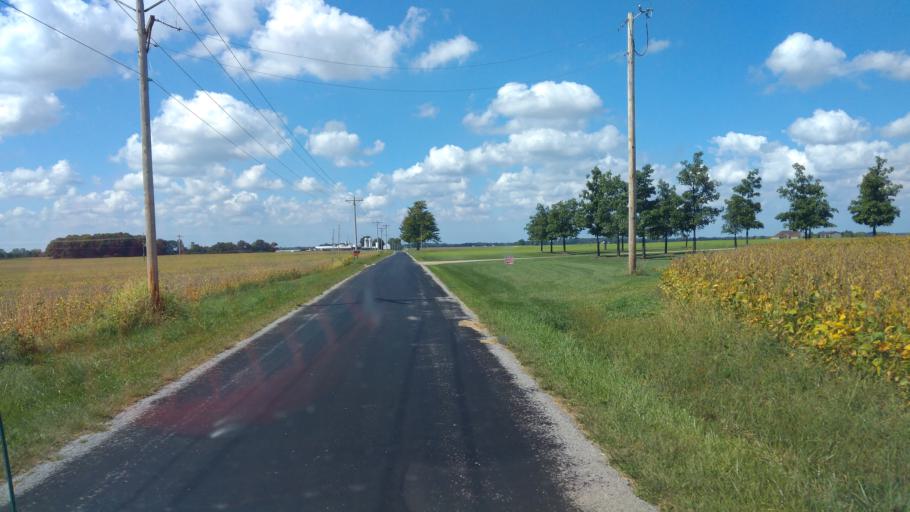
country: US
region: Ohio
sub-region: Marion County
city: Marion
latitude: 40.6587
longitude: -83.2640
